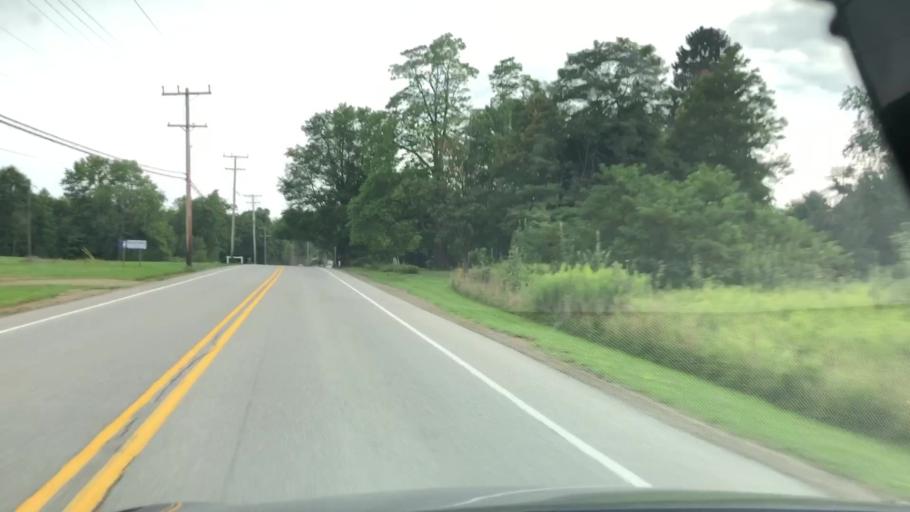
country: US
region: Pennsylvania
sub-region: Crawford County
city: Titusville
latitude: 41.5587
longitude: -79.6963
